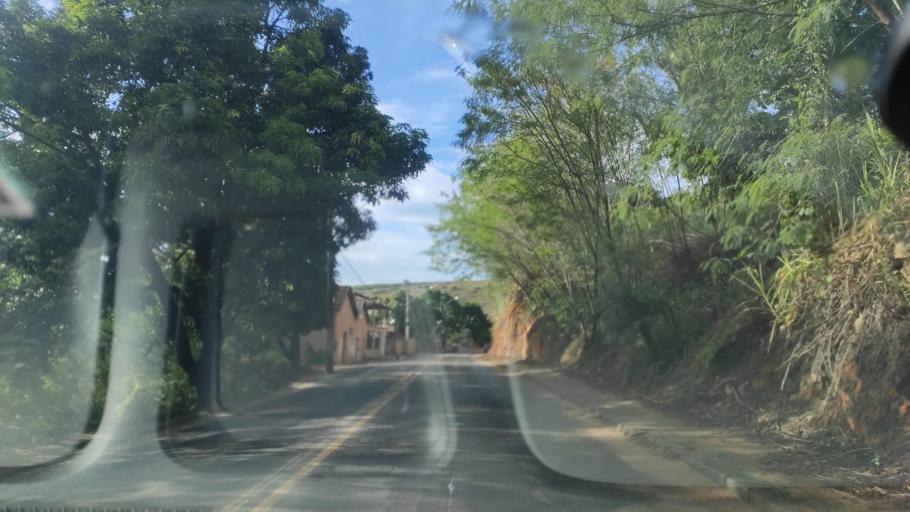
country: BR
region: Espirito Santo
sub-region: Nova Venecia
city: Nova Venecia
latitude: -18.7131
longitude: -40.3900
